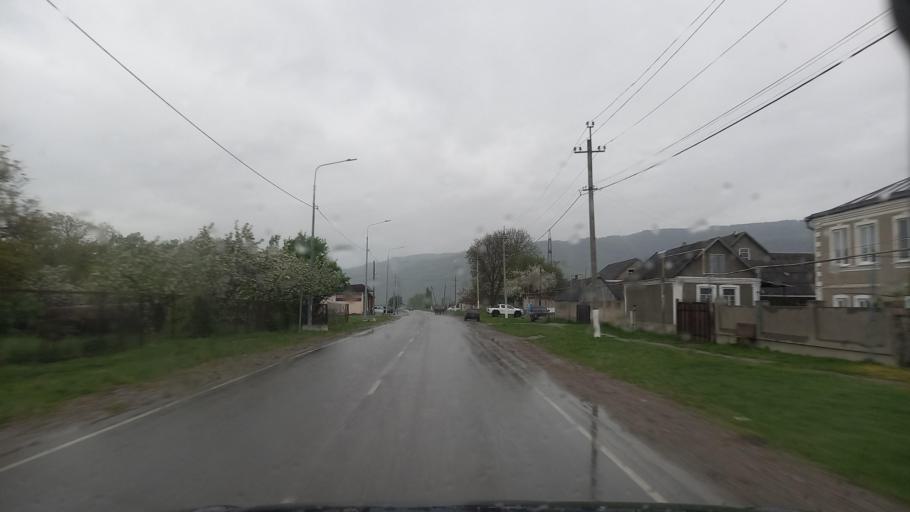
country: RU
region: Kabardino-Balkariya
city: Zhankhoteko
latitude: 43.5884
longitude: 43.2149
